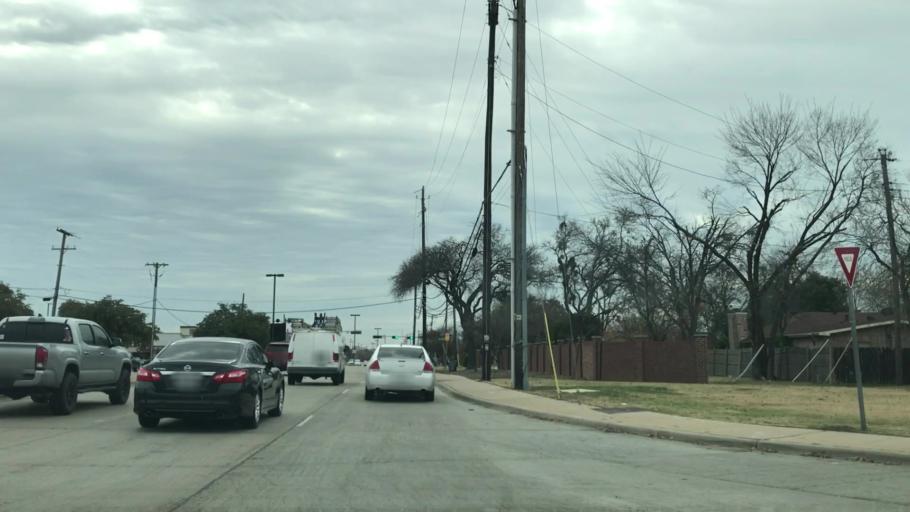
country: US
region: Texas
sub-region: Dallas County
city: Carrollton
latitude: 32.9535
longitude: -96.8904
